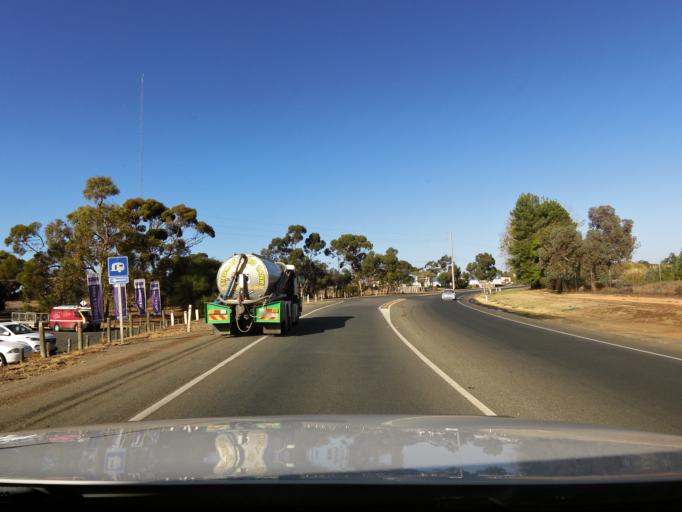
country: AU
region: South Australia
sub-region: Berri and Barmera
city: Berri
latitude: -34.2633
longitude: 140.6140
